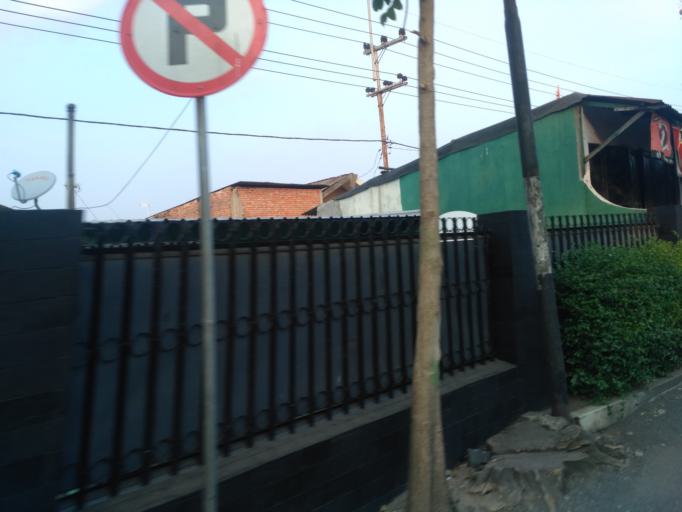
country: ID
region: East Java
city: Kepuh
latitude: -8.0082
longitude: 112.6193
